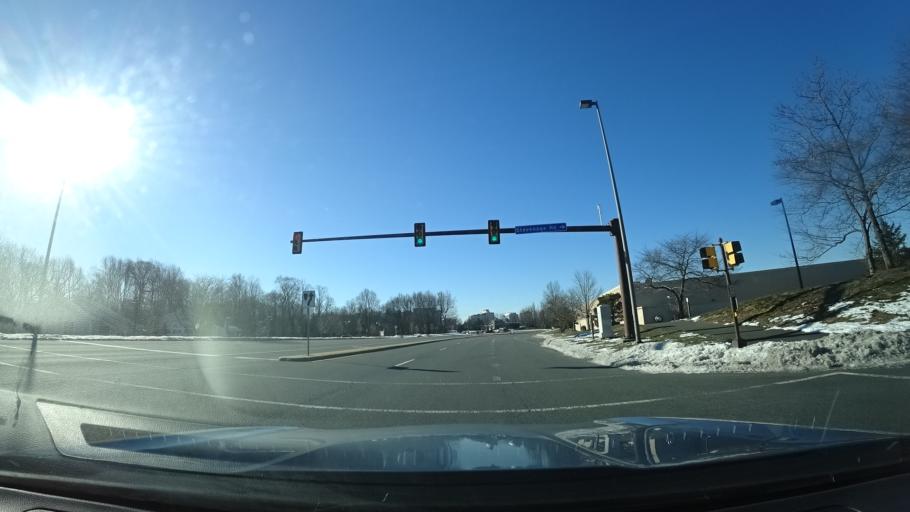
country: US
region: Virginia
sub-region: Fairfax County
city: Reston
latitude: 38.9693
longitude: -77.3525
